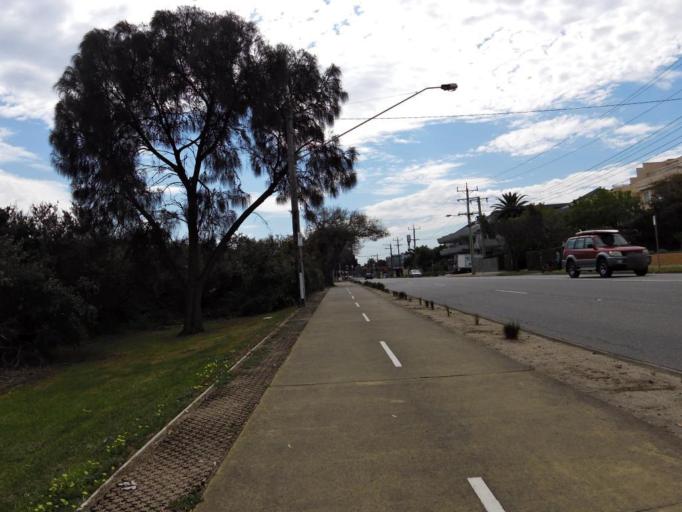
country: AU
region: Victoria
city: Hampton
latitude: -37.9470
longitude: 145.0006
